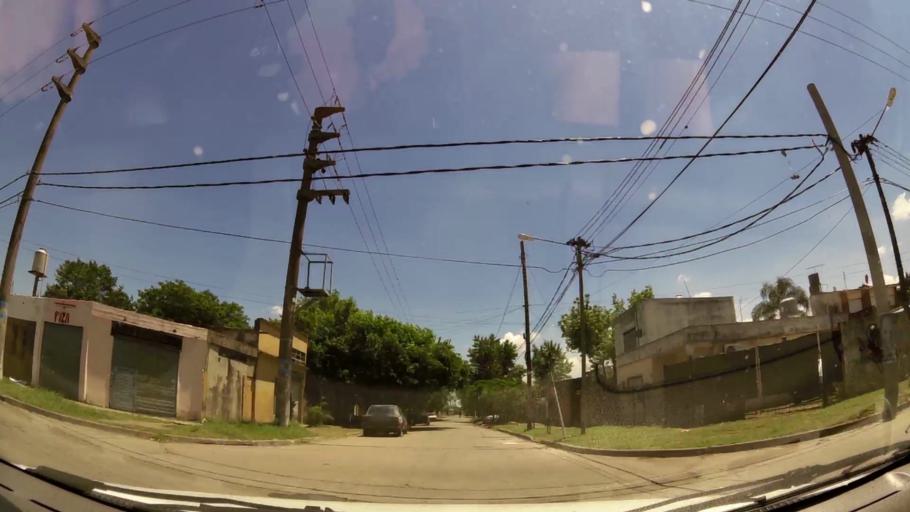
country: AR
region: Buenos Aires
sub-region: Partido de Merlo
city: Merlo
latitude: -34.6448
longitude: -58.7100
